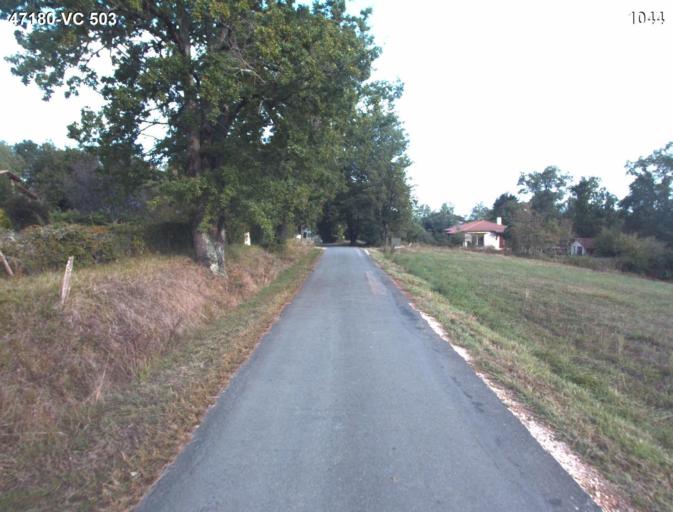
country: FR
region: Aquitaine
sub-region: Departement du Lot-et-Garonne
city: Sainte-Colombe-en-Bruilhois
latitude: 44.1745
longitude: 0.4329
